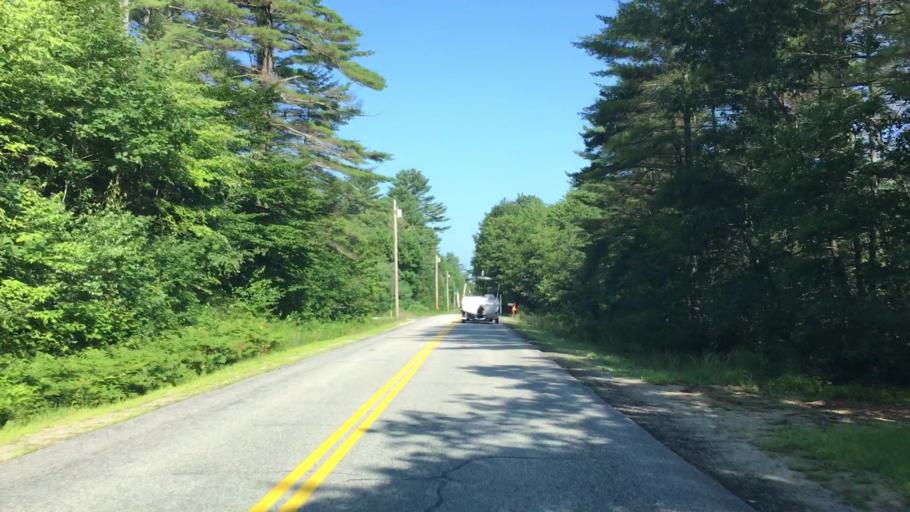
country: US
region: Maine
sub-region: Androscoggin County
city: Poland
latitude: 44.0496
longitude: -70.3676
